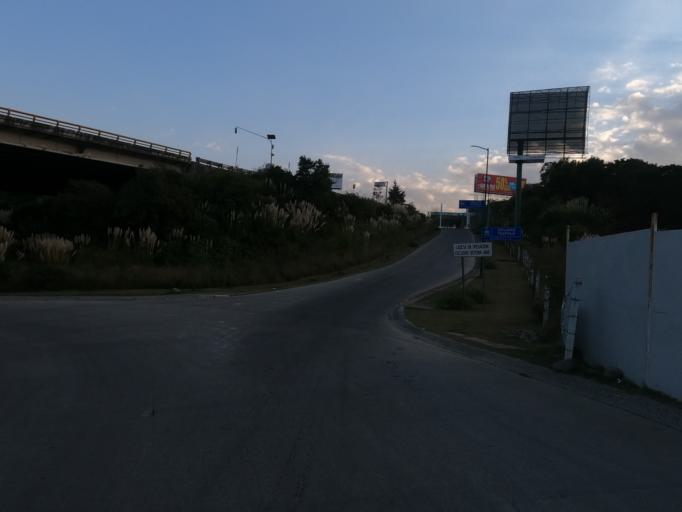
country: MX
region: Mexico
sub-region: Naucalpan de Juarez
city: Ejido el Castillo
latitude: 19.4209
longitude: -99.3001
